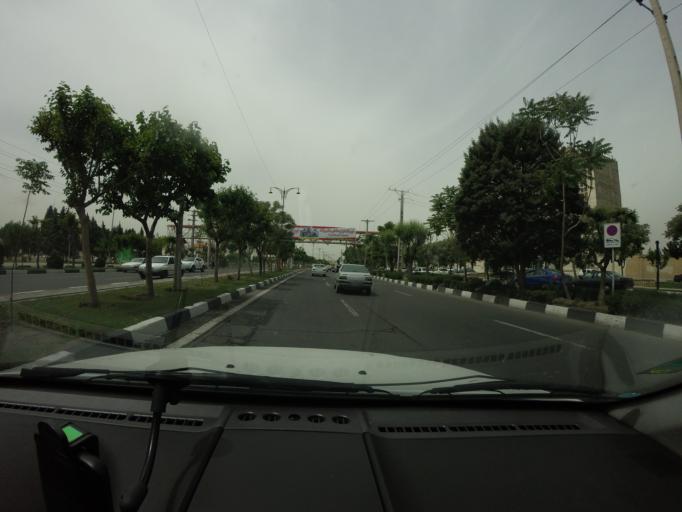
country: IR
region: Tehran
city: Eslamshahr
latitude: 35.5599
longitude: 51.2506
